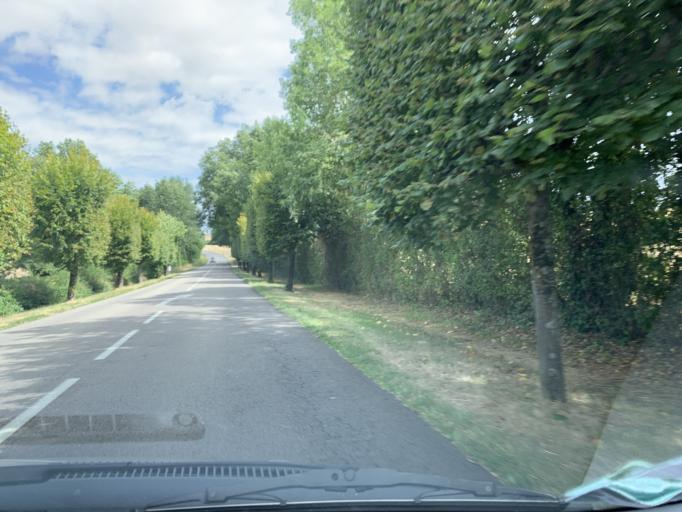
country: FR
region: Bourgogne
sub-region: Departement de la Nievre
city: Varzy
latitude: 47.3601
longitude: 3.3939
